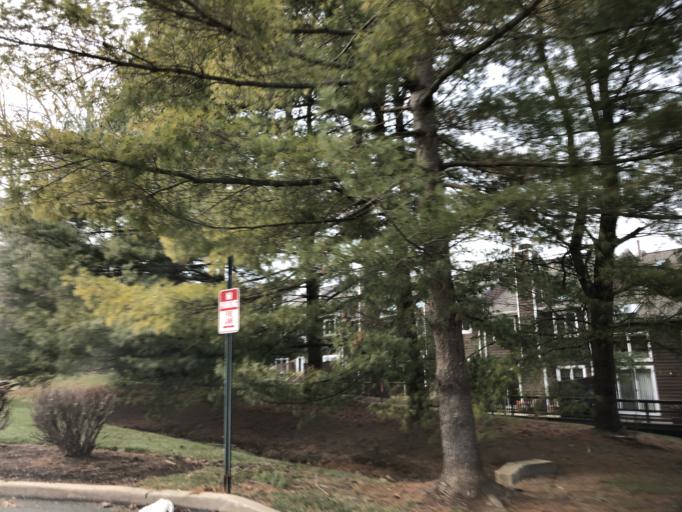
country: US
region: Pennsylvania
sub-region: Chester County
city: Exton
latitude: 40.0349
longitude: -75.6396
